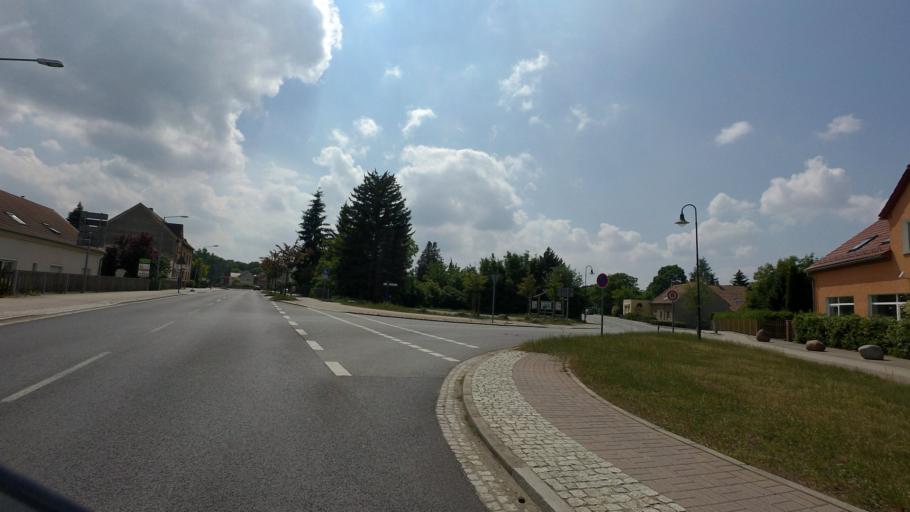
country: DE
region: Saxony
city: Rietschen
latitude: 51.3955
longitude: 14.7858
